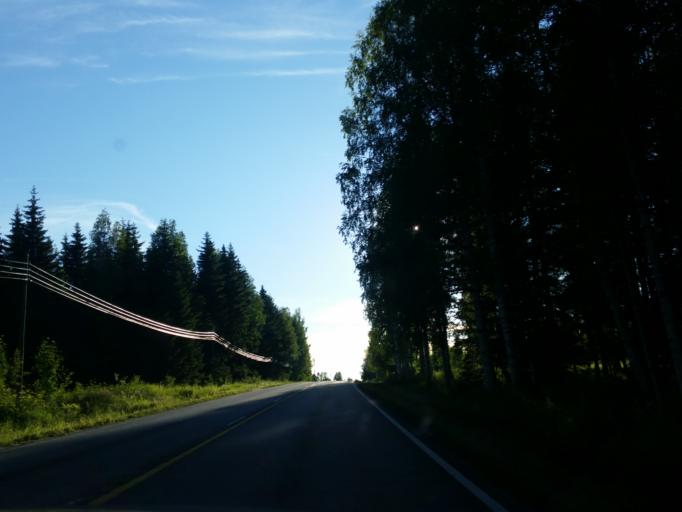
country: FI
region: Northern Savo
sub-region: Kuopio
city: Kuopio
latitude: 62.8456
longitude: 27.4045
